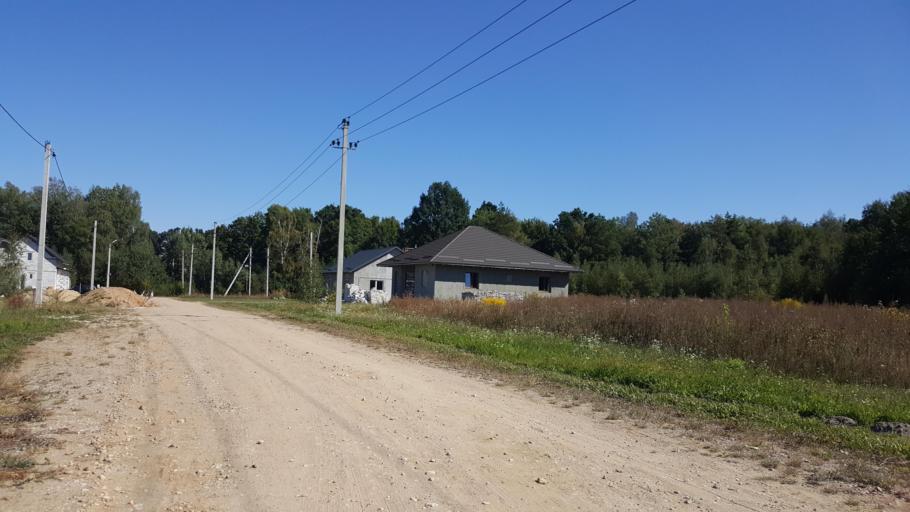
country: BY
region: Brest
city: Vysokaye
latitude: 52.2499
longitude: 23.5022
